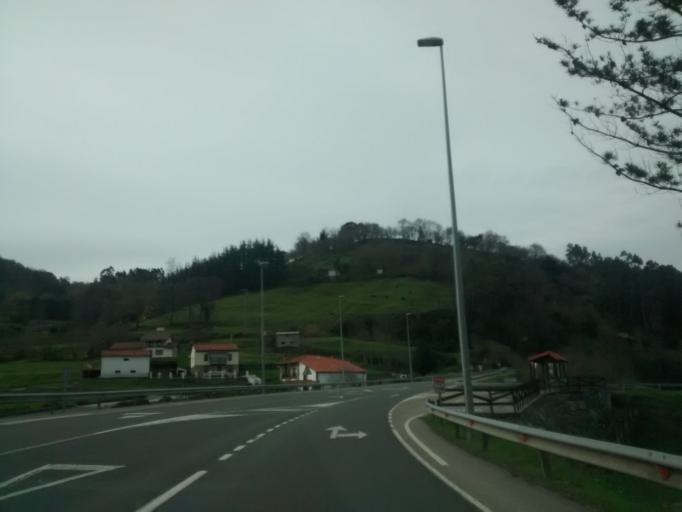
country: ES
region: Cantabria
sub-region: Provincia de Cantabria
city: Santiurde de Toranzo
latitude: 43.2357
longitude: -3.9475
